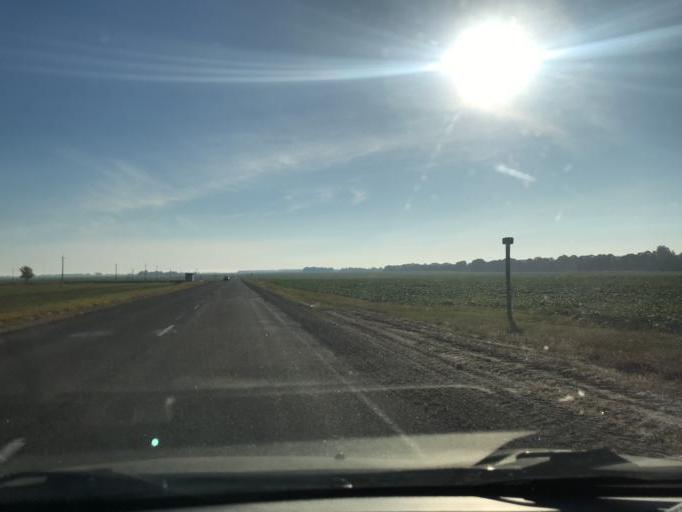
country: BY
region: Gomel
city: Brahin
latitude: 51.7980
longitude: 30.1397
